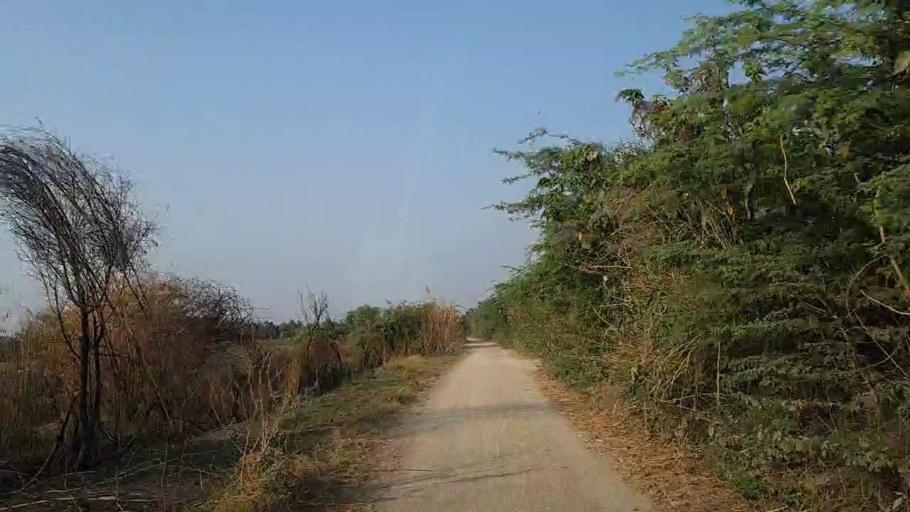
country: PK
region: Sindh
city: Thatta
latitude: 24.6747
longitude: 67.7835
